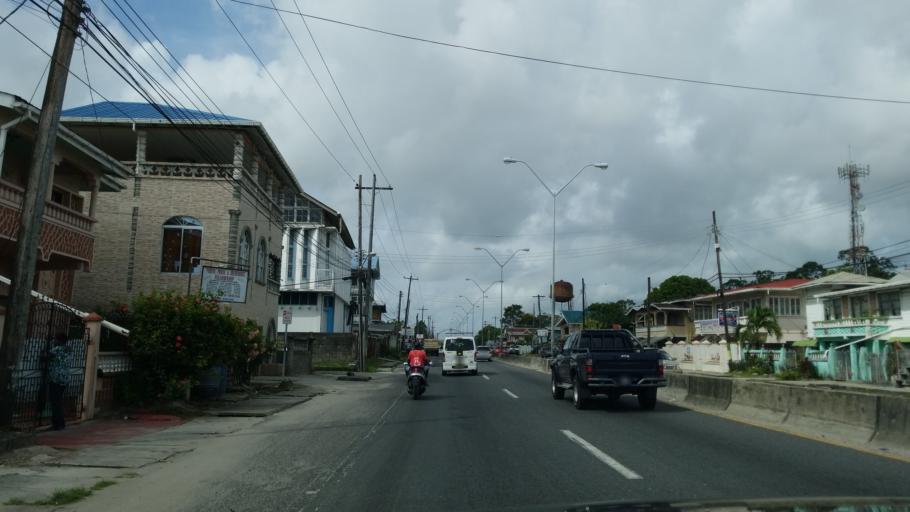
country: GY
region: Demerara-Mahaica
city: Georgetown
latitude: 6.7816
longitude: -58.1700
